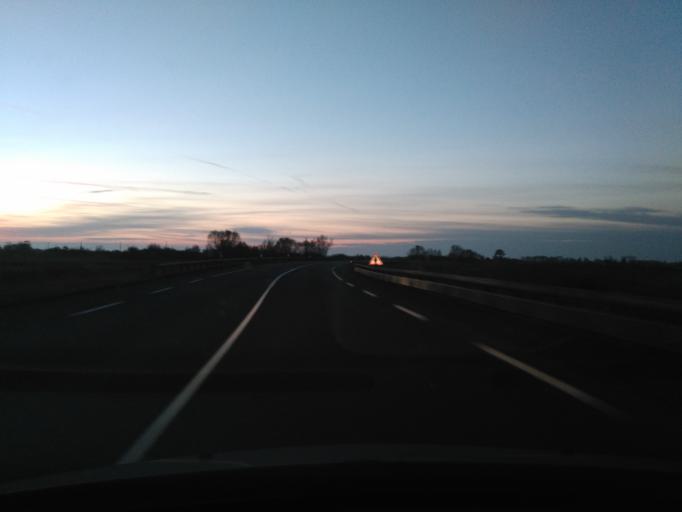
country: FR
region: Pays de la Loire
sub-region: Departement de la Vendee
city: Champagne-les-Marais
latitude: 46.4175
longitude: -1.1015
